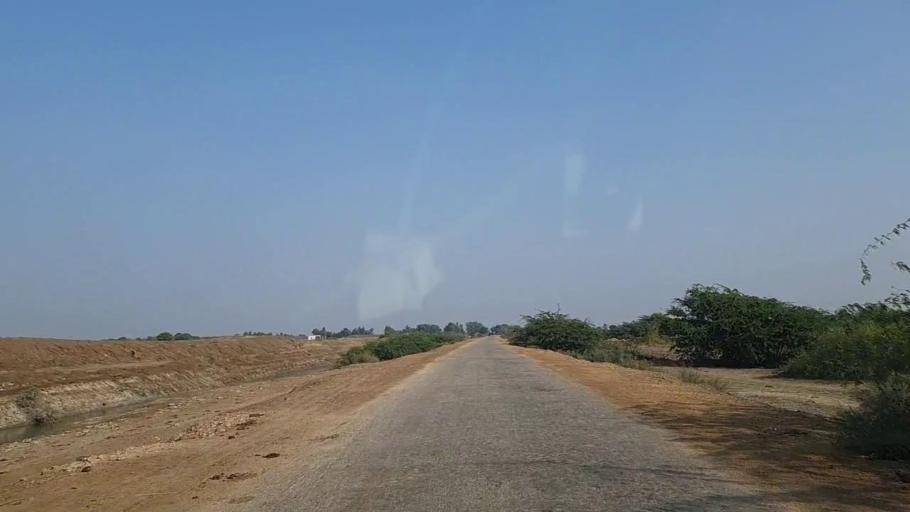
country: PK
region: Sindh
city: Mirpur Sakro
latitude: 24.6290
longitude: 67.6438
